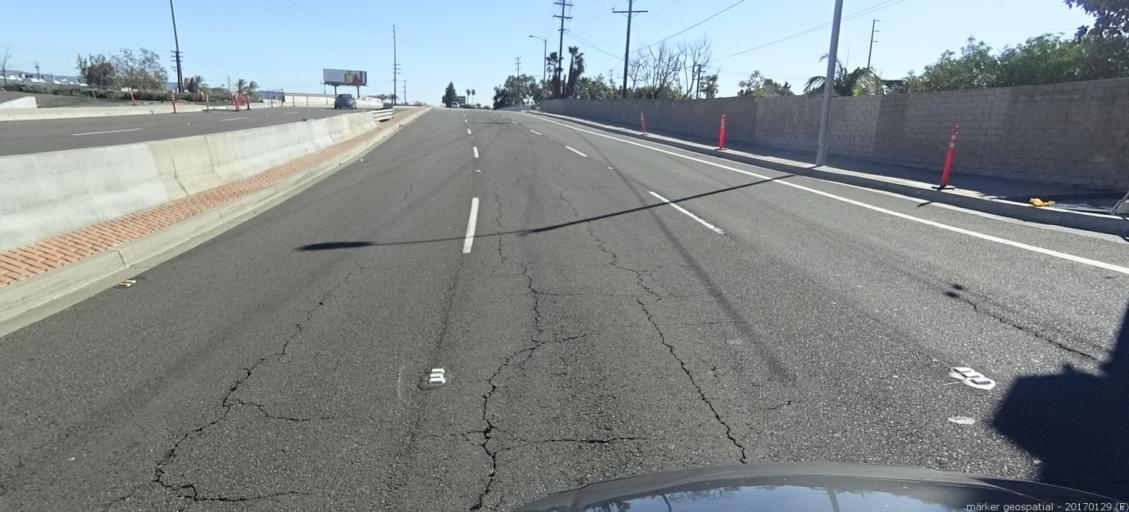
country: US
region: California
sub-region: Orange County
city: Fountain Valley
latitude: 33.7179
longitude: -117.9212
